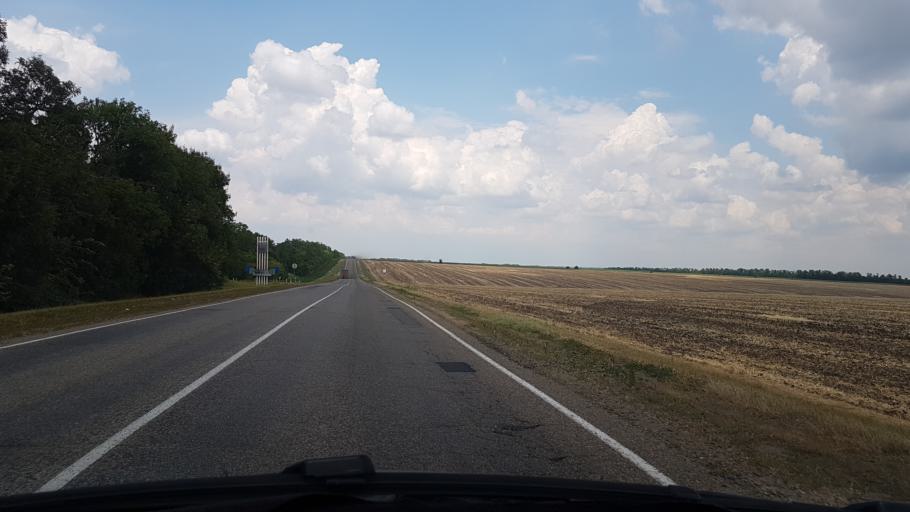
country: RU
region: Krasnodarskiy
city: Dmitriyevskaya
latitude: 45.6724
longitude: 40.7441
